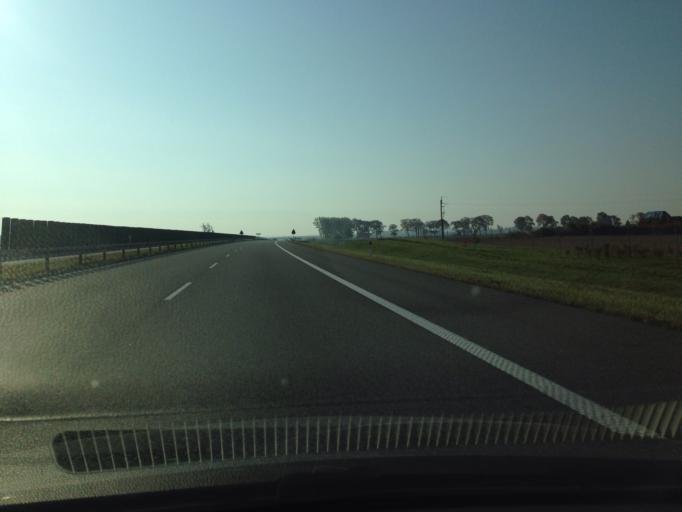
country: PL
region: Pomeranian Voivodeship
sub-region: Powiat gdanski
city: Pszczolki
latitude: 54.1402
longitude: 18.6736
